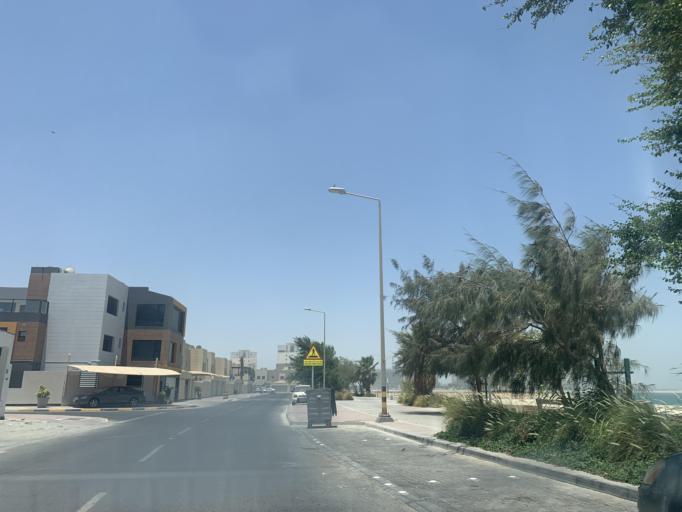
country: BH
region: Manama
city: Jidd Hafs
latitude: 26.2389
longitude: 50.4690
